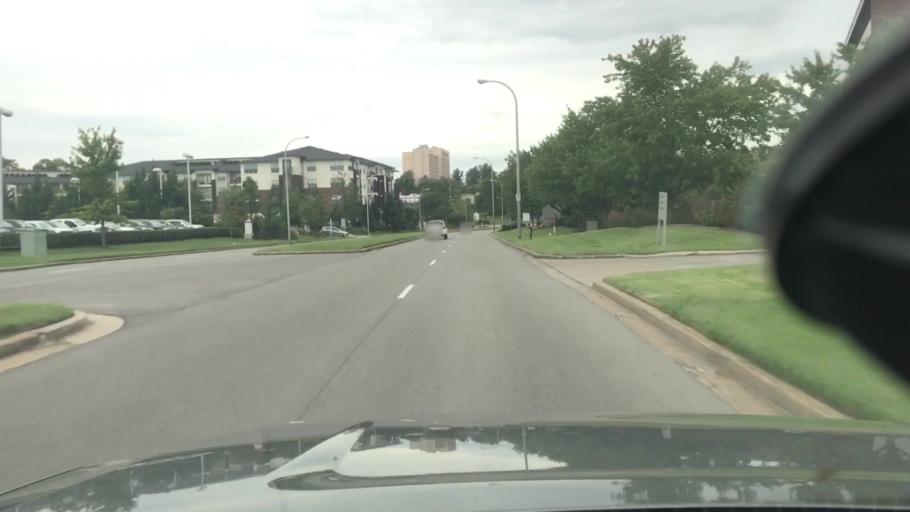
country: US
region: Tennessee
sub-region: Davidson County
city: Nashville
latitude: 36.1921
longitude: -86.7931
